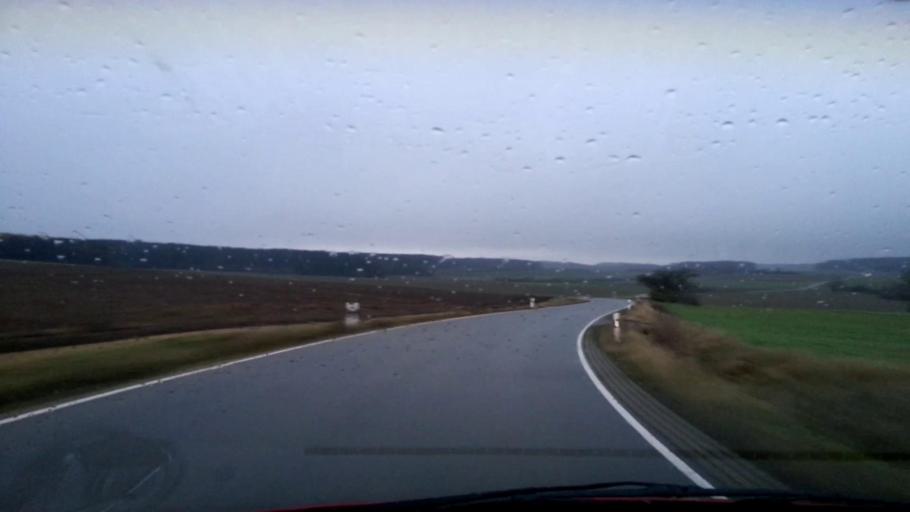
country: DE
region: Bavaria
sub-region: Upper Franconia
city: Konigsfeld
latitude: 49.9499
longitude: 11.1530
